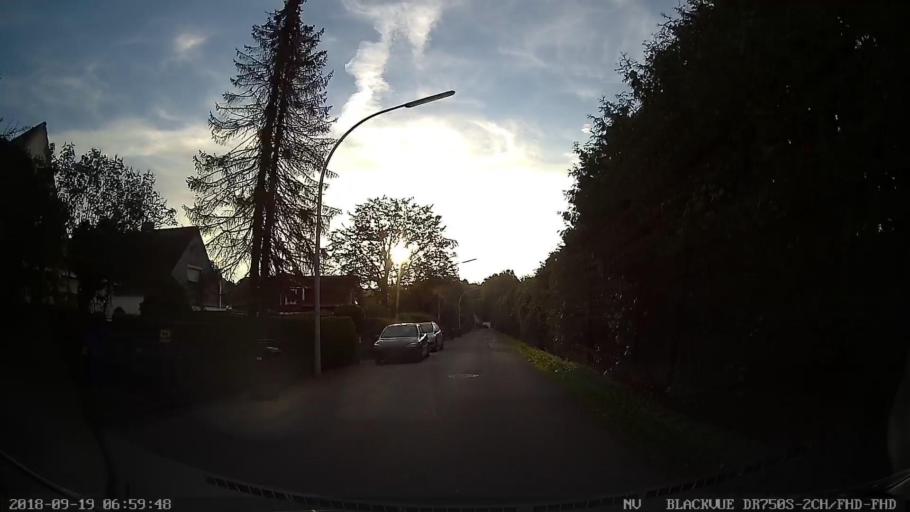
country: DE
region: Hamburg
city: Eidelstedt
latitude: 53.6326
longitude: 9.8929
